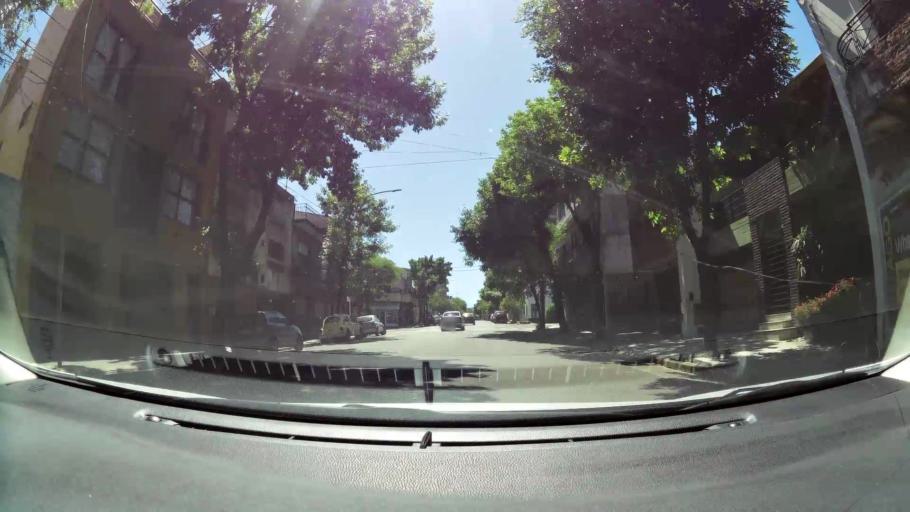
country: AR
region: Buenos Aires F.D.
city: Buenos Aires
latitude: -34.6291
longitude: -58.4114
